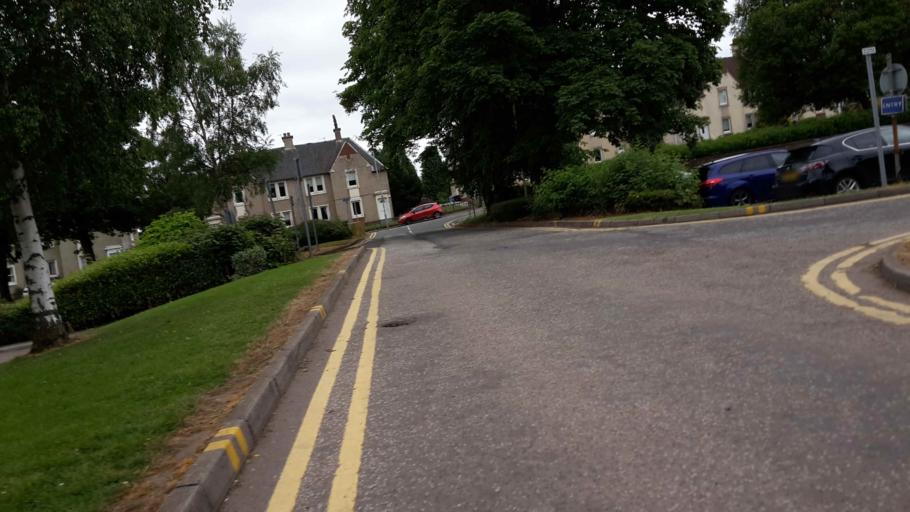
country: GB
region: Scotland
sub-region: South Lanarkshire
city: High Blantyre
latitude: 55.7933
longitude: -4.0863
